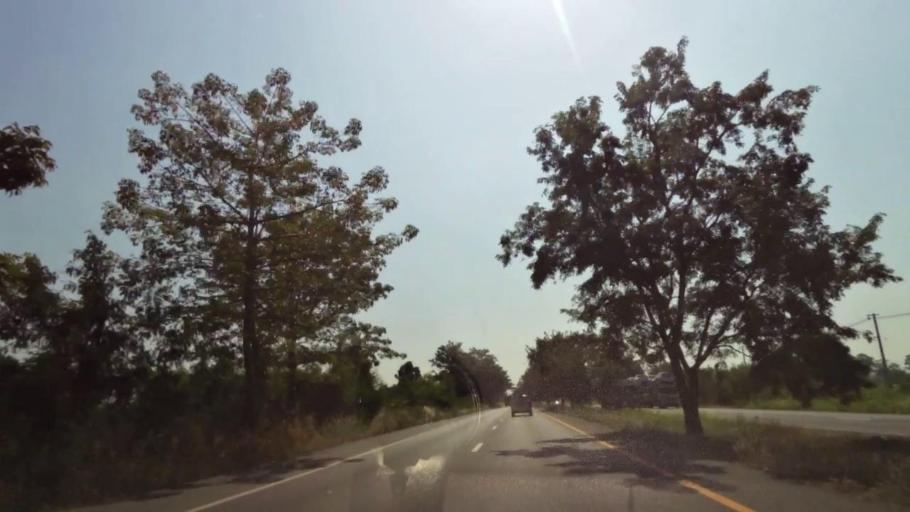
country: TH
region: Nakhon Sawan
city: Kao Liao
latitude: 15.9472
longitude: 100.1150
